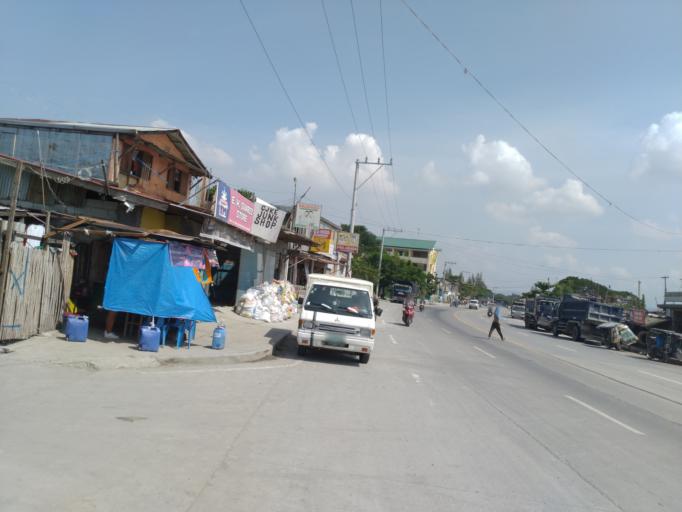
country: PH
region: Calabarzon
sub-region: Province of Rizal
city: Taytay
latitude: 14.5369
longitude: 121.1119
